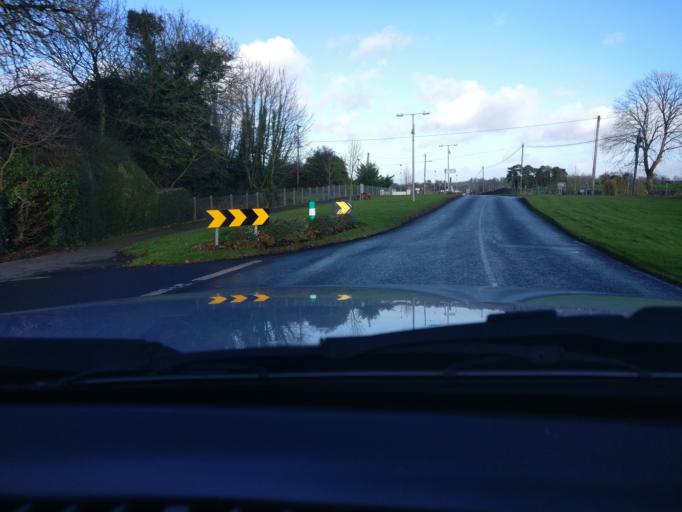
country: IE
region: Leinster
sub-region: An Iarmhi
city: Kilbeggan
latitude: 53.4299
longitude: -7.5596
